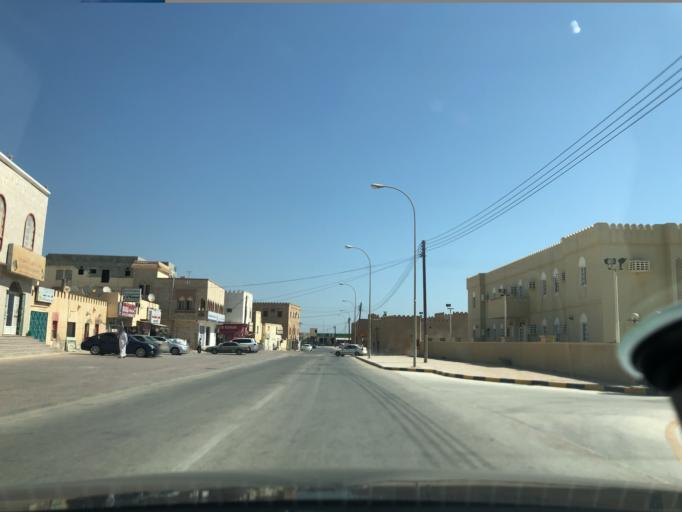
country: OM
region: Zufar
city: Salalah
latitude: 17.0381
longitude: 54.3925
